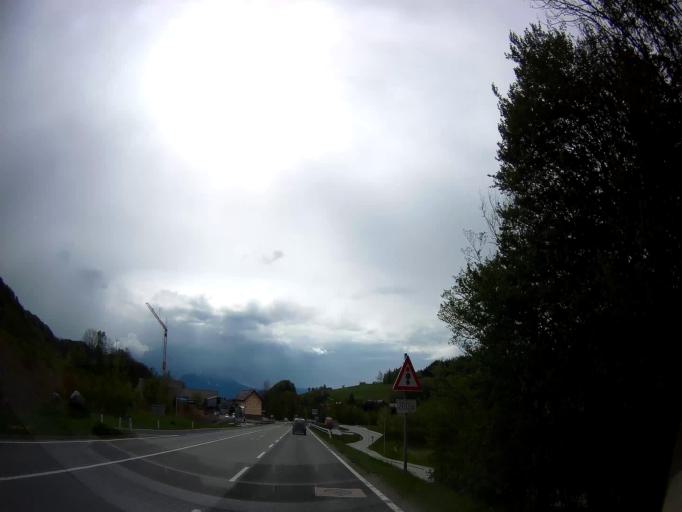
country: AT
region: Salzburg
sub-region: Politischer Bezirk Salzburg-Umgebung
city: Hallwang
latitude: 47.8183
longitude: 13.1041
